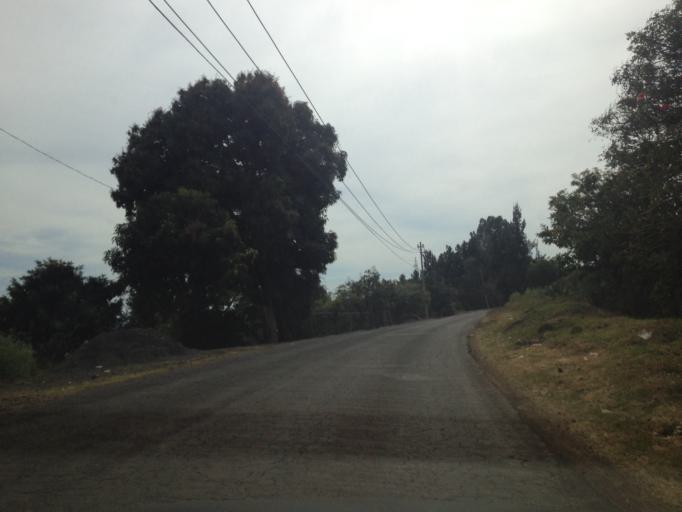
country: MX
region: Michoacan
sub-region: Ziracuaretiro
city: Patuan
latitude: 19.4288
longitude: -101.9237
